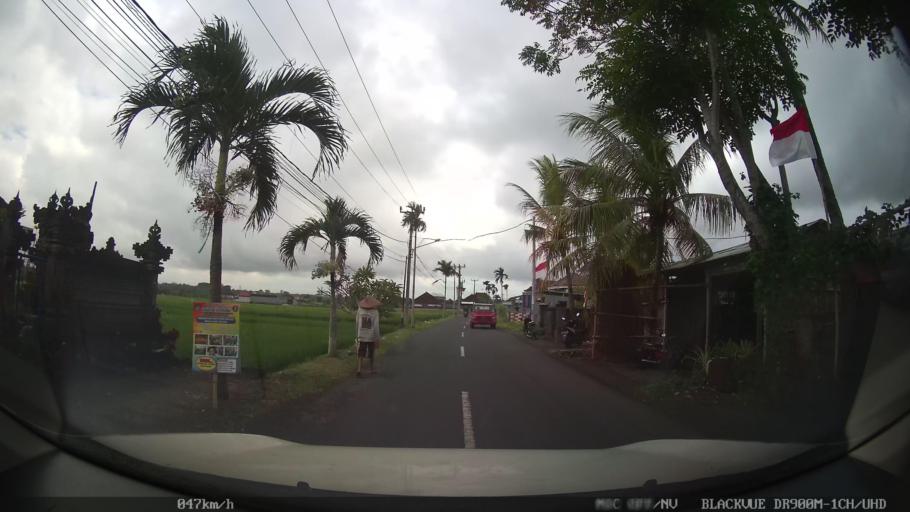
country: ID
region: Bali
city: Banjar Mambalkajanan
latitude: -8.5481
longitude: 115.2124
